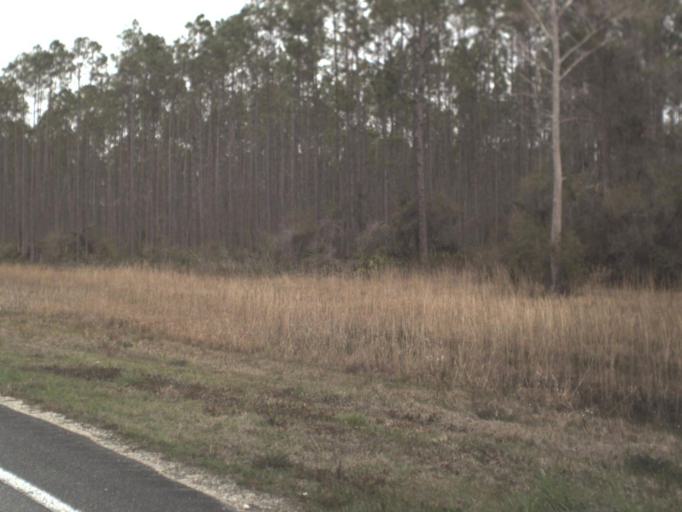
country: US
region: Florida
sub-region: Leon County
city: Woodville
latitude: 30.1958
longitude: -84.1455
